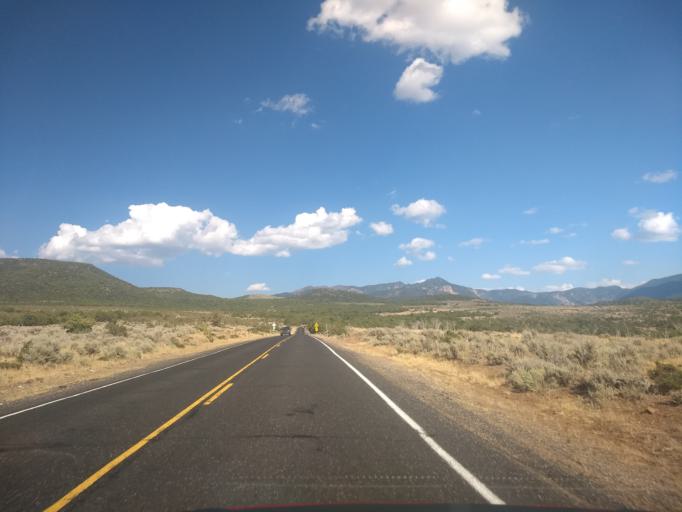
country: US
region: Utah
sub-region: Washington County
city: Enterprise
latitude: 37.4184
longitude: -113.5541
